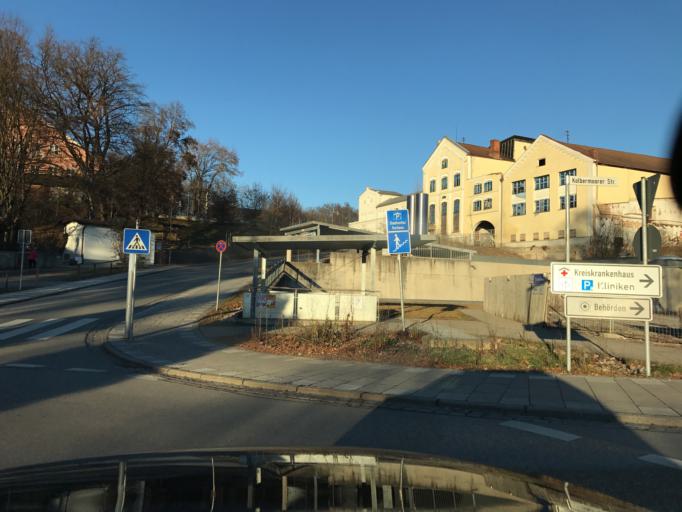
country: DE
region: Bavaria
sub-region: Upper Bavaria
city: Bad Aibling
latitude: 47.8625
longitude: 12.0121
